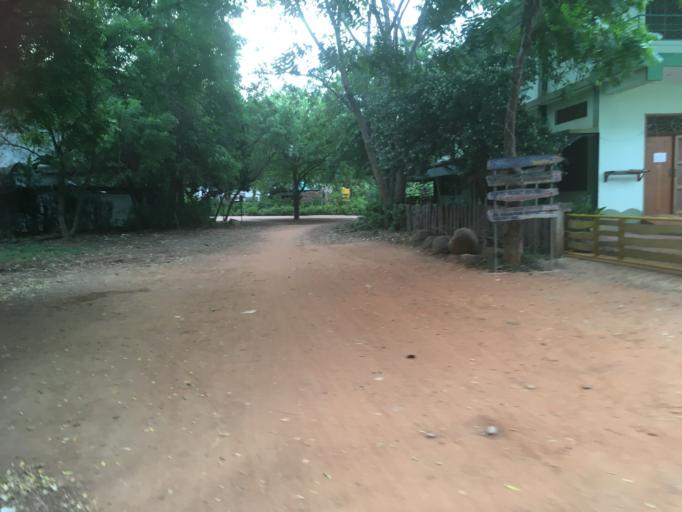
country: IN
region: Tamil Nadu
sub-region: Villupuram
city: Auroville
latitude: 12.0150
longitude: 79.8018
